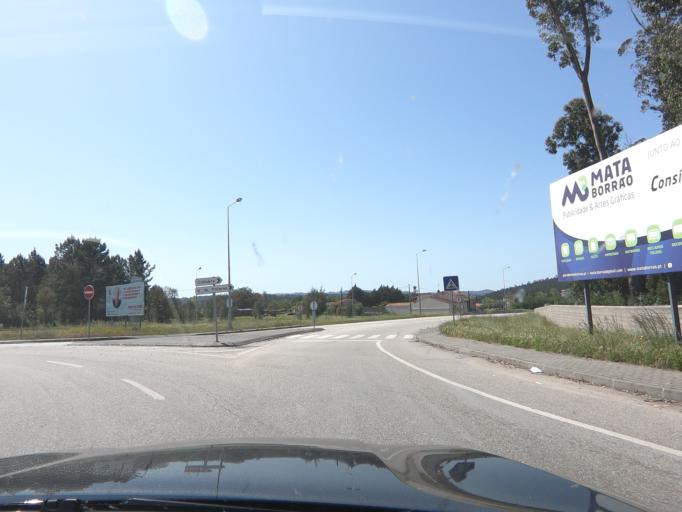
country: PT
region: Coimbra
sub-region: Lousa
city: Lousa
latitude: 40.1364
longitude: -8.2504
